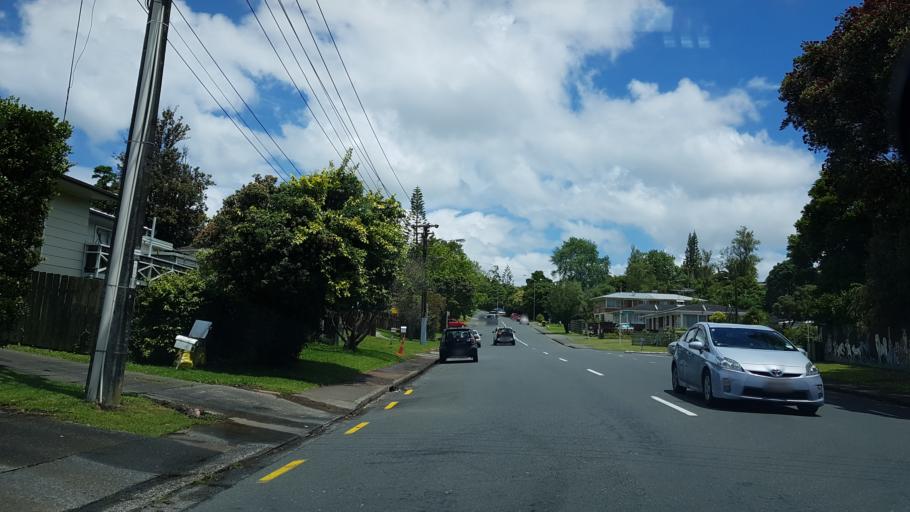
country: NZ
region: Auckland
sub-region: Auckland
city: North Shore
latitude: -36.7760
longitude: 174.7322
